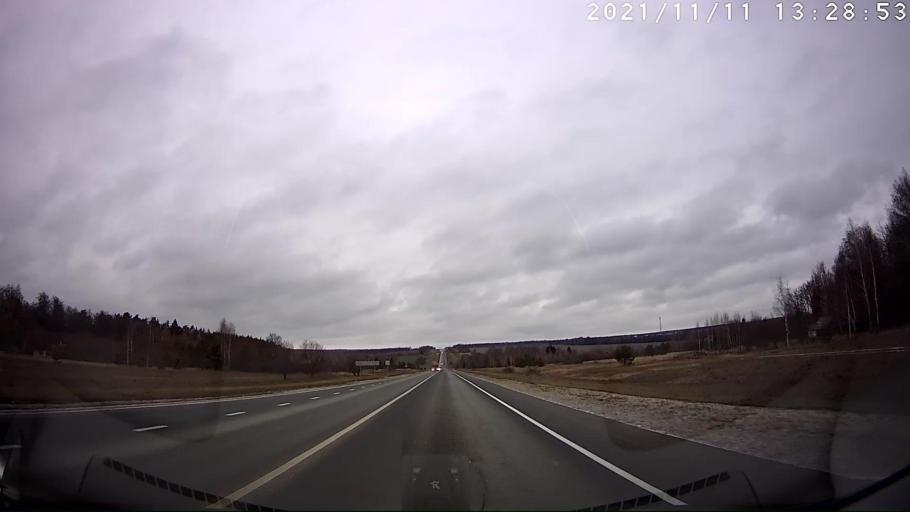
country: RU
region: Chuvashia
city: Komsomol'skoye
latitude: 55.3007
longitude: 47.5555
